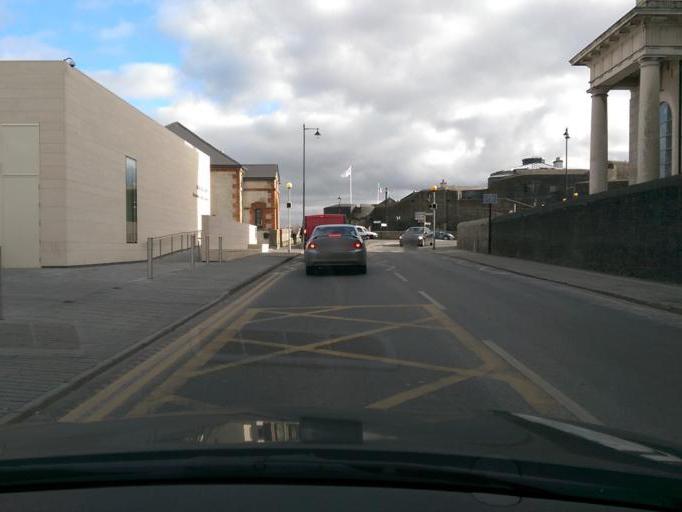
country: IE
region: Leinster
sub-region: An Iarmhi
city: Athlone
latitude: 53.4241
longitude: -7.9434
